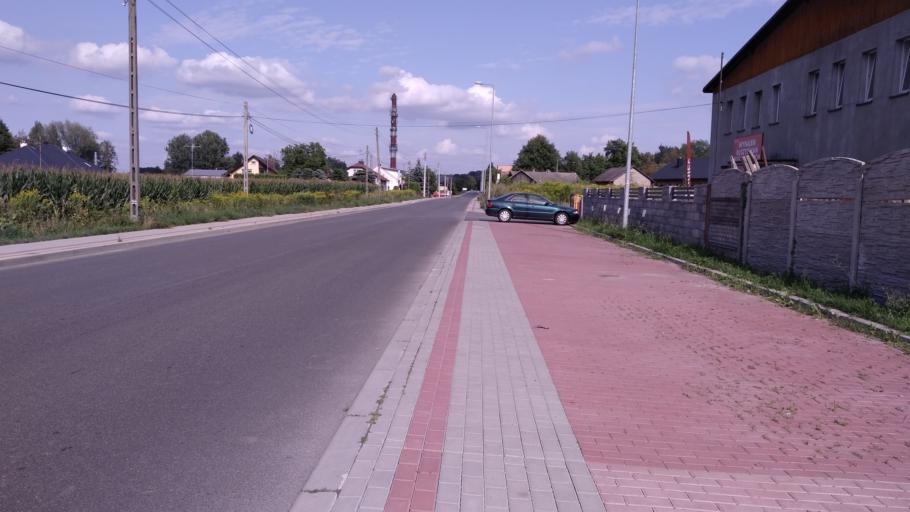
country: PL
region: Subcarpathian Voivodeship
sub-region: Powiat lancucki
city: Lancut
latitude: 50.0788
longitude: 22.2169
